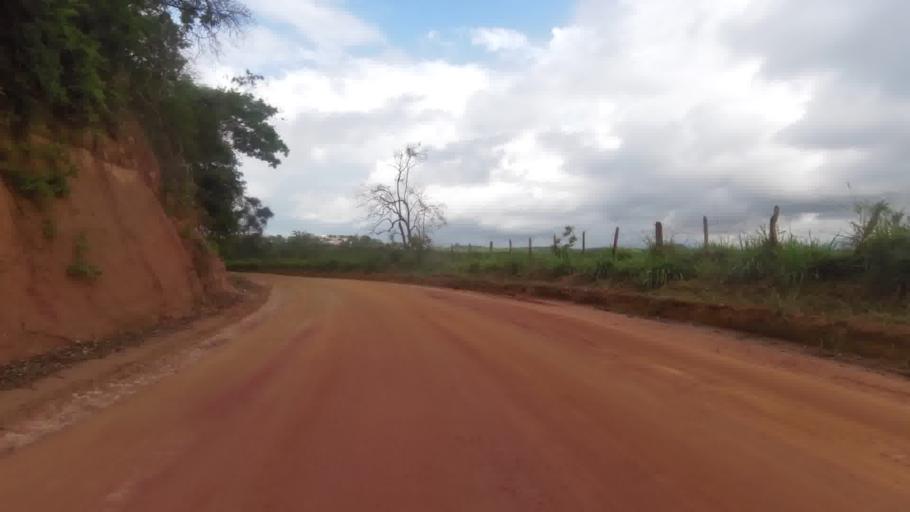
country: BR
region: Espirito Santo
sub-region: Piuma
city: Piuma
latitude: -20.7865
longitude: -40.6324
